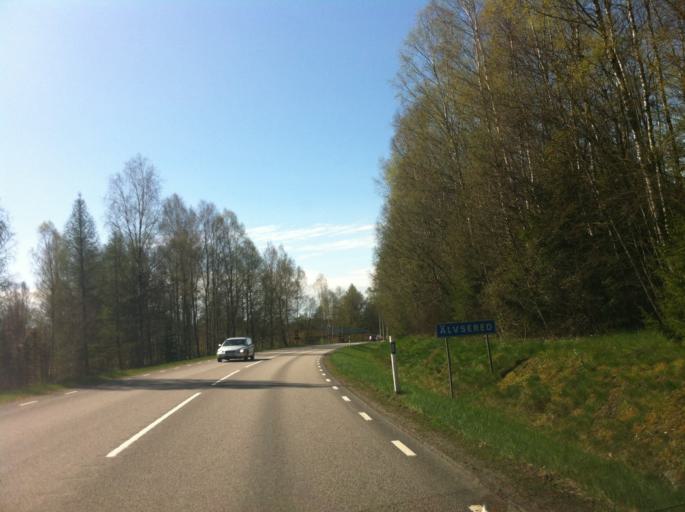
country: SE
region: Vaestra Goetaland
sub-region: Marks Kommun
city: Kinna
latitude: 57.2463
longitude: 12.8665
